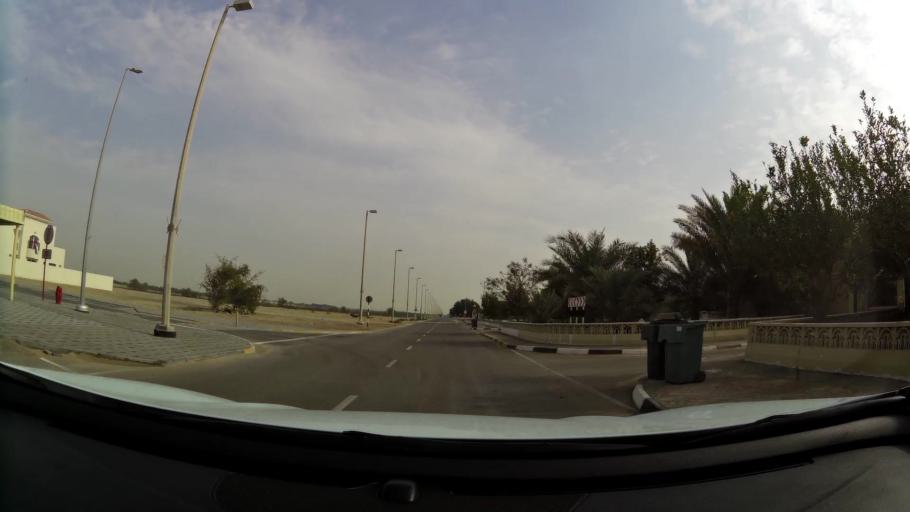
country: AE
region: Abu Dhabi
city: Abu Dhabi
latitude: 24.6723
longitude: 54.7499
